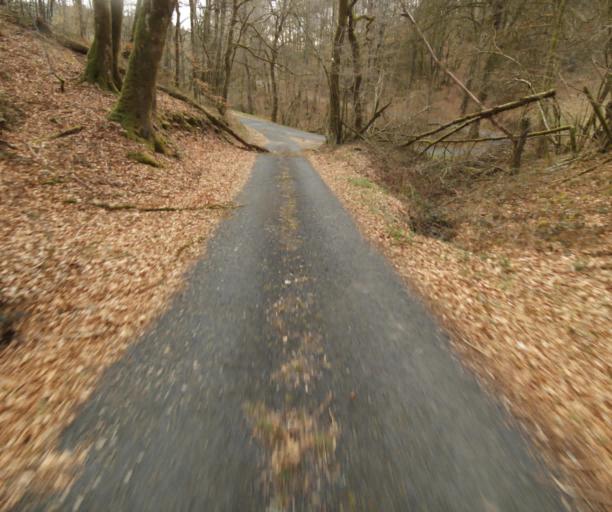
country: FR
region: Limousin
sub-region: Departement de la Correze
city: Correze
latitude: 45.3907
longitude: 1.8871
